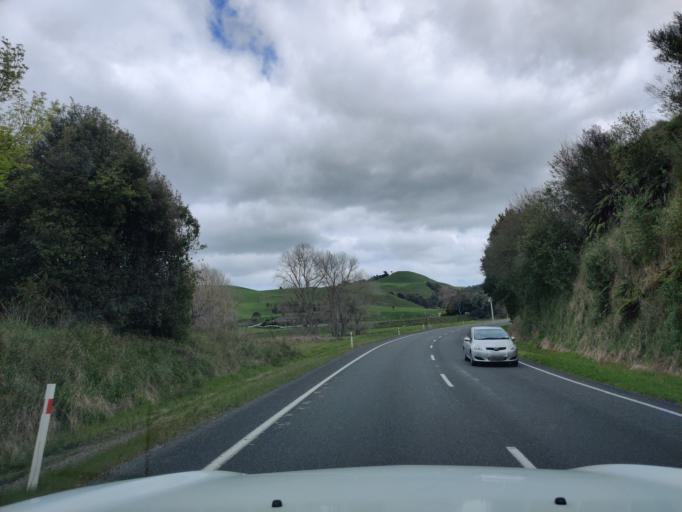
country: NZ
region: Manawatu-Wanganui
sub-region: Wanganui District
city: Wanganui
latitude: -39.8478
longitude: 175.1415
